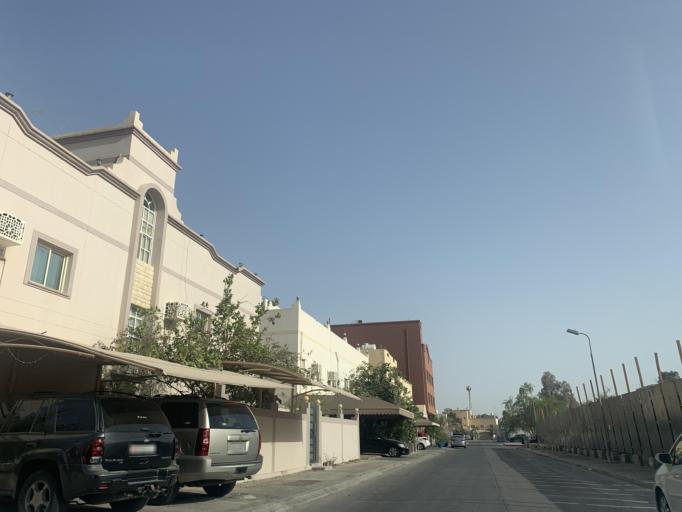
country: BH
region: Manama
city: Jidd Hafs
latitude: 26.2280
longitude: 50.5470
